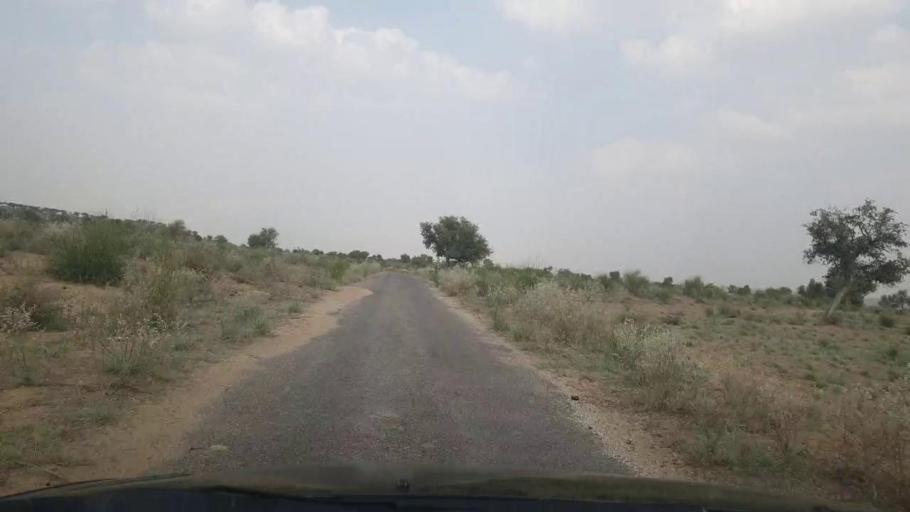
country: PK
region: Sindh
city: Islamkot
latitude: 24.9134
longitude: 70.5615
